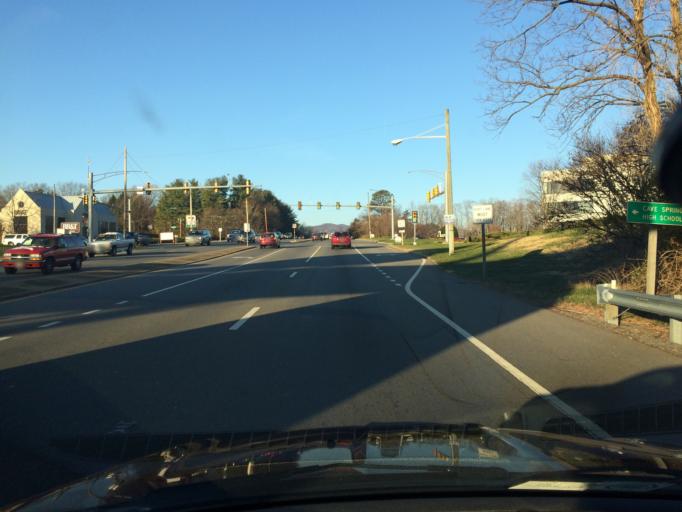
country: US
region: Virginia
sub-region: Roanoke County
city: Cave Spring
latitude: 37.2243
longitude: -79.9899
